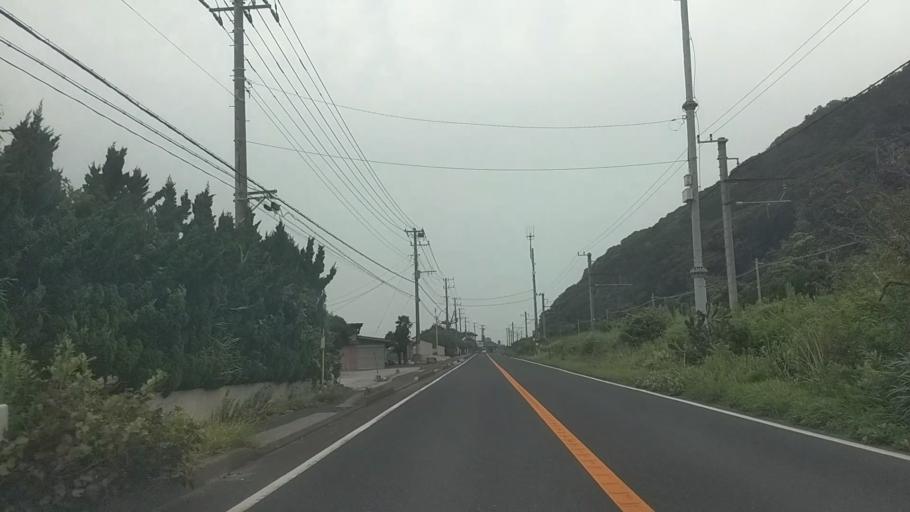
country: JP
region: Chiba
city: Futtsu
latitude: 35.1864
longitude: 139.8191
